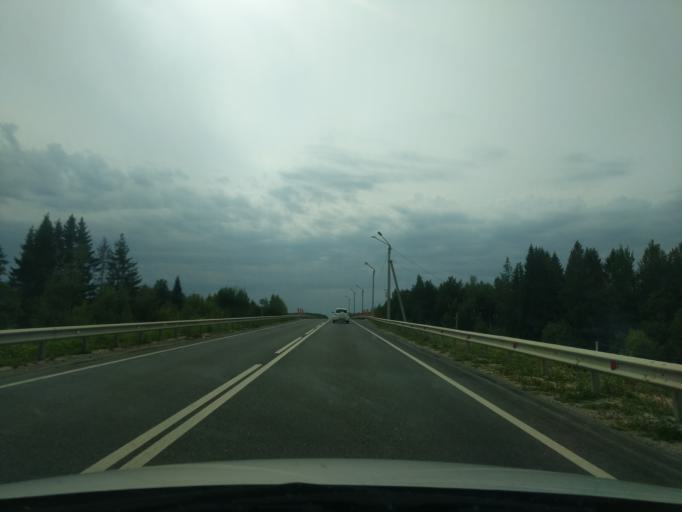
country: RU
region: Kostroma
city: Manturovo
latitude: 58.3307
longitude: 44.7164
